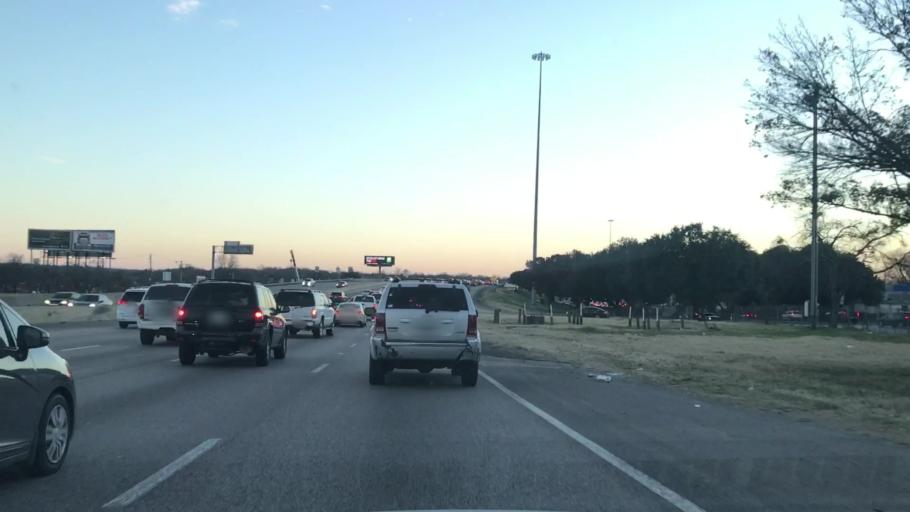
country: US
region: Texas
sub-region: Dallas County
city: Dallas
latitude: 32.7371
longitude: -96.8242
